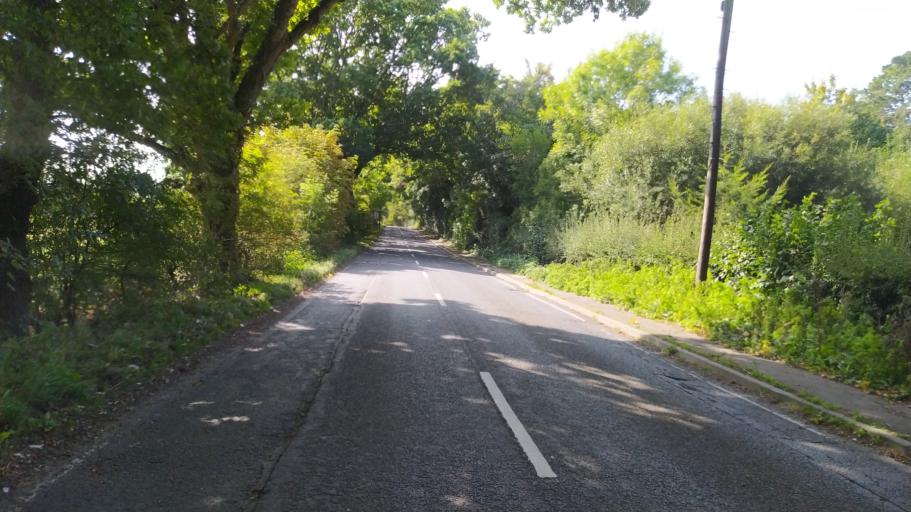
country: GB
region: England
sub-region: Hampshire
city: Botley
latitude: 50.9188
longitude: -1.2547
